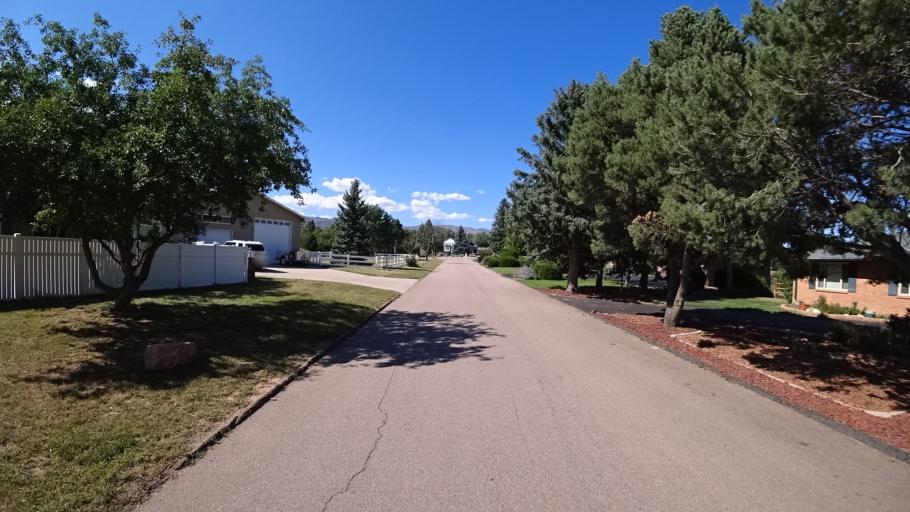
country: US
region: Colorado
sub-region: El Paso County
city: Colorado Springs
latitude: 38.8648
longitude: -104.8577
